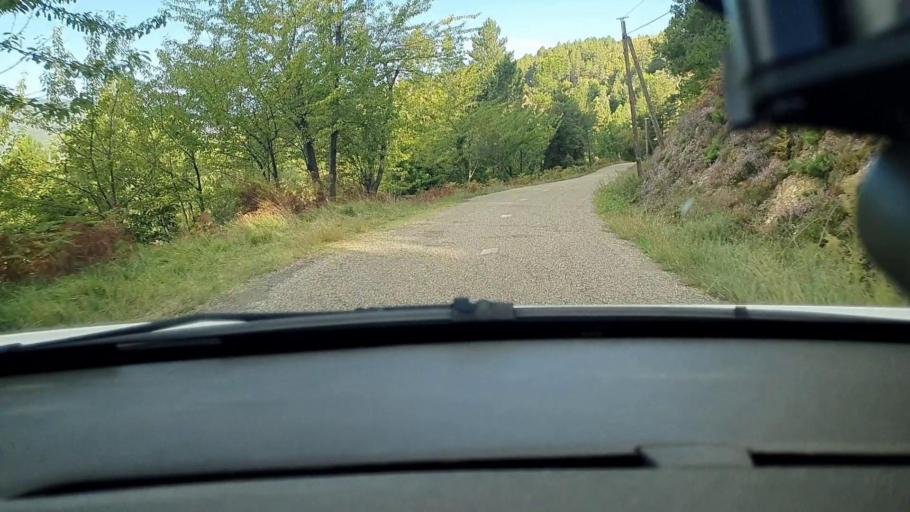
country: FR
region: Languedoc-Roussillon
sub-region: Departement du Gard
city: Besseges
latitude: 44.3306
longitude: 3.9992
